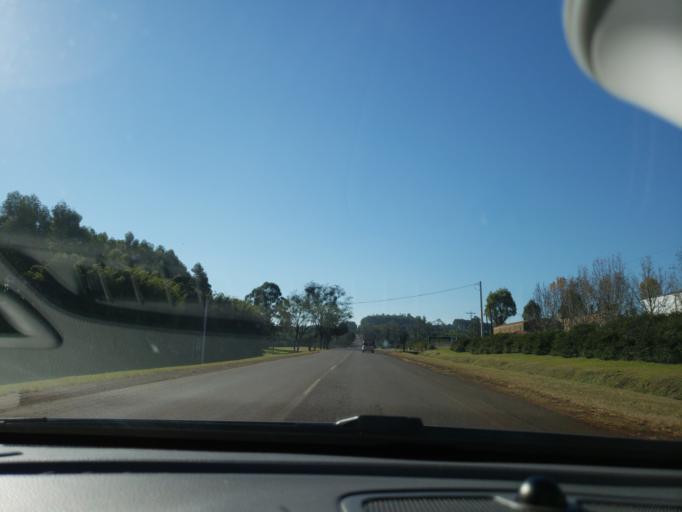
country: AR
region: Misiones
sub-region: Departamento de Apostoles
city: San Jose
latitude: -27.8133
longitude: -55.7688
